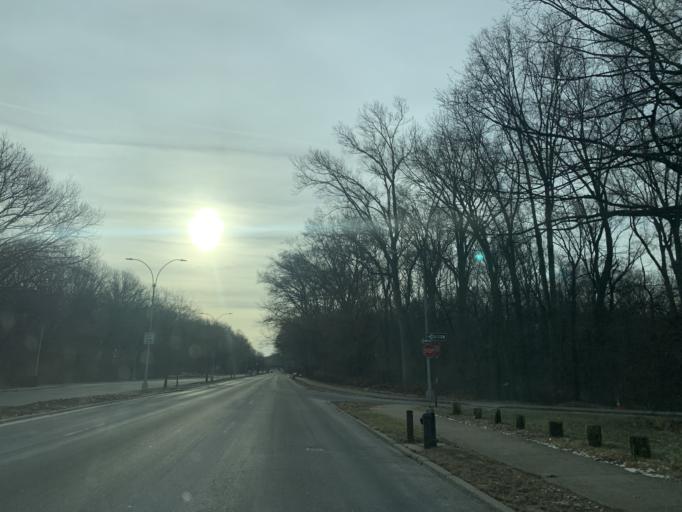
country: US
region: New York
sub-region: Nassau County
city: Bellerose Terrace
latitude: 40.7304
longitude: -73.7692
